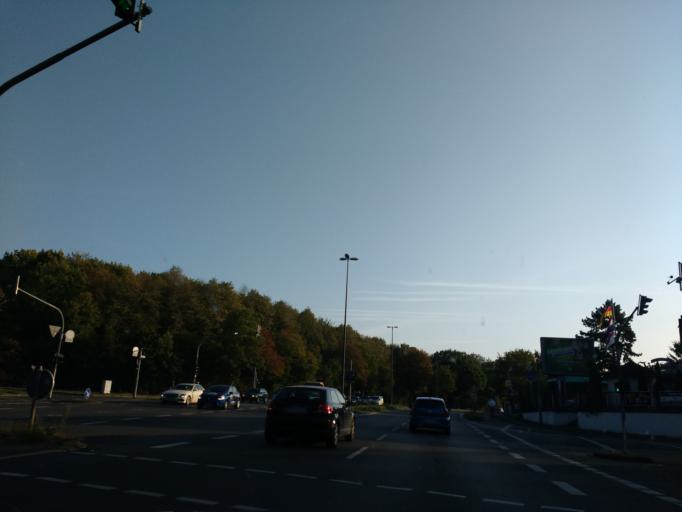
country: DE
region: North Rhine-Westphalia
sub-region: Regierungsbezirk Koln
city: Bilderstoeckchen
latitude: 50.9985
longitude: 6.9021
